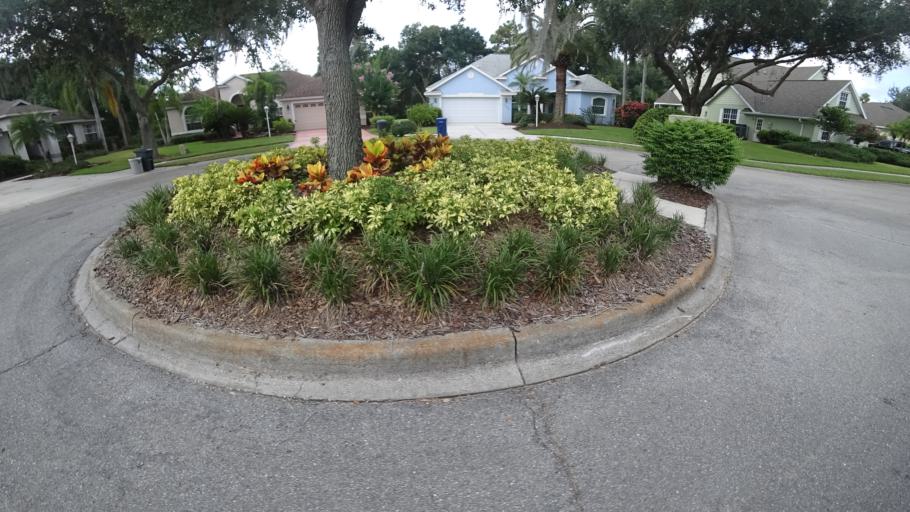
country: US
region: Florida
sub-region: Sarasota County
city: The Meadows
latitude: 27.4203
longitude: -82.4277
